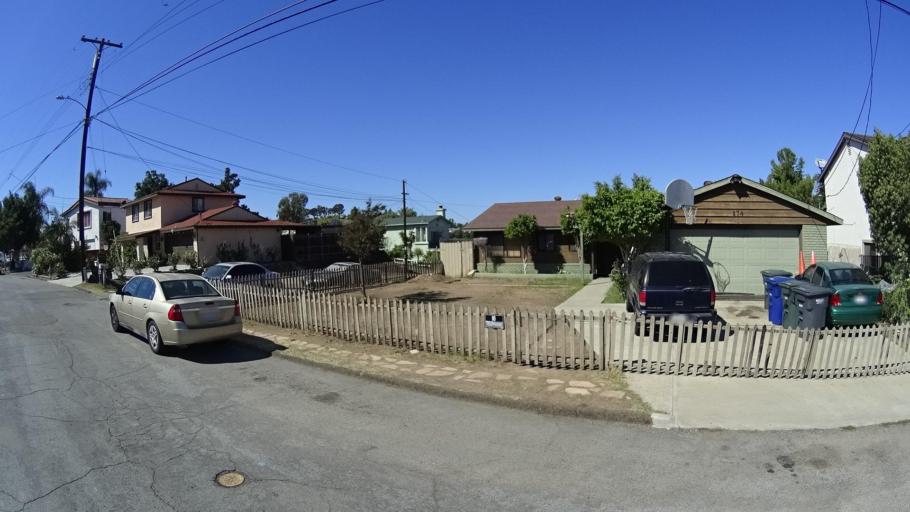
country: US
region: California
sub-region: San Diego County
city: La Presa
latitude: 32.6987
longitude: -117.0056
